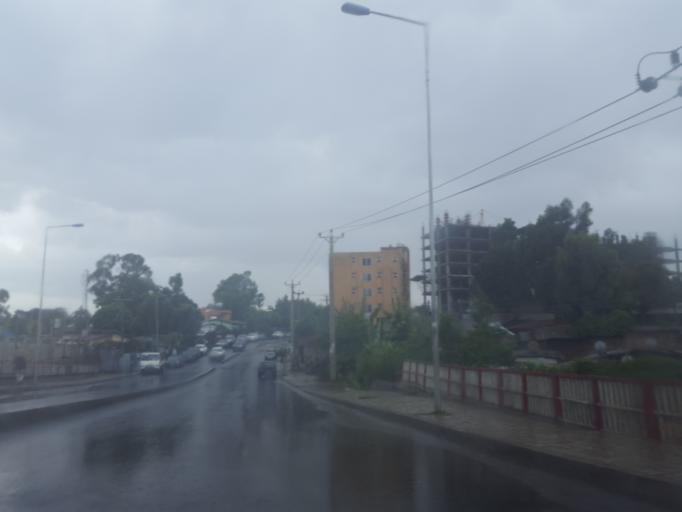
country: ET
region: Adis Abeba
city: Addis Ababa
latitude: 9.0284
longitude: 38.7807
